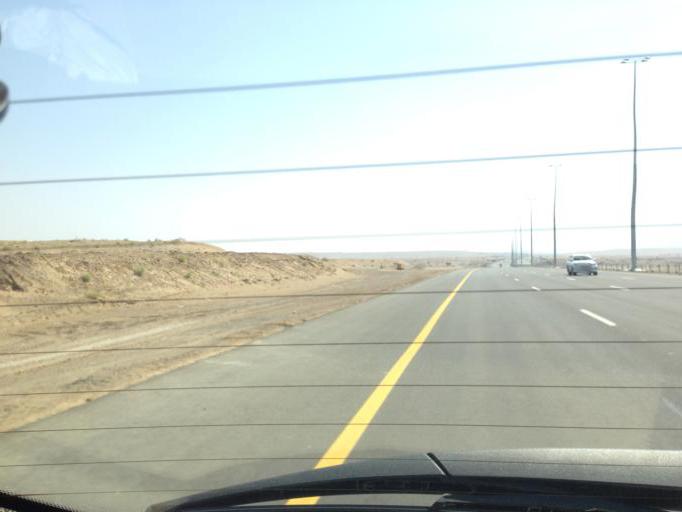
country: OM
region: Al Batinah
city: Rustaq
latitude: 23.5296
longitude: 57.5928
